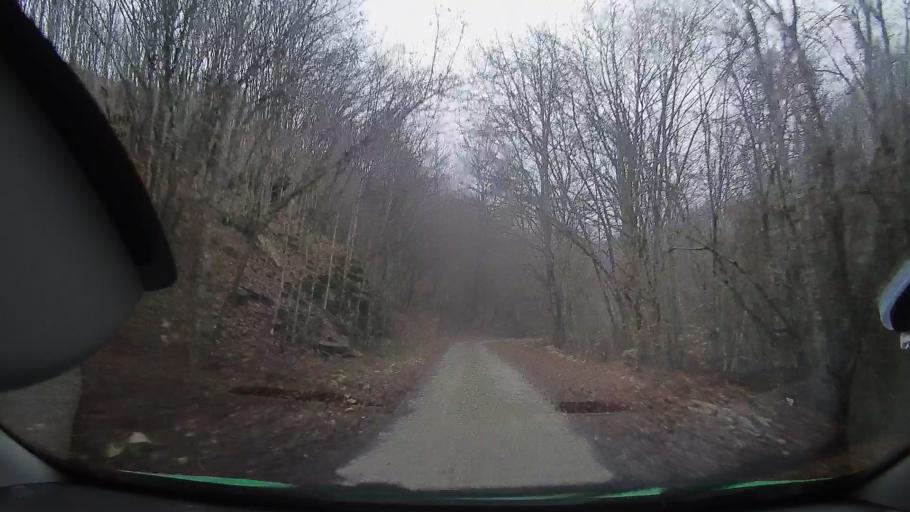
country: RO
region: Alba
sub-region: Comuna Avram Iancu
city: Avram Iancu
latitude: 46.3111
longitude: 22.7838
